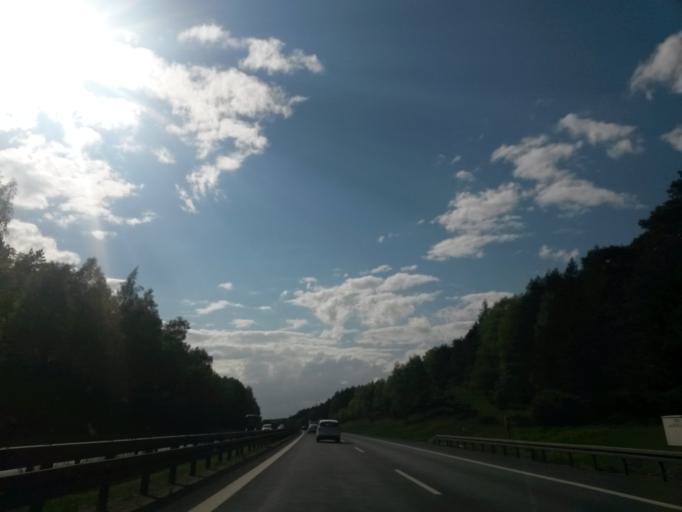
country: DE
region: Bavaria
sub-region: Regierungsbezirk Mittelfranken
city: Rohr
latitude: 49.3144
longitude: 10.8918
